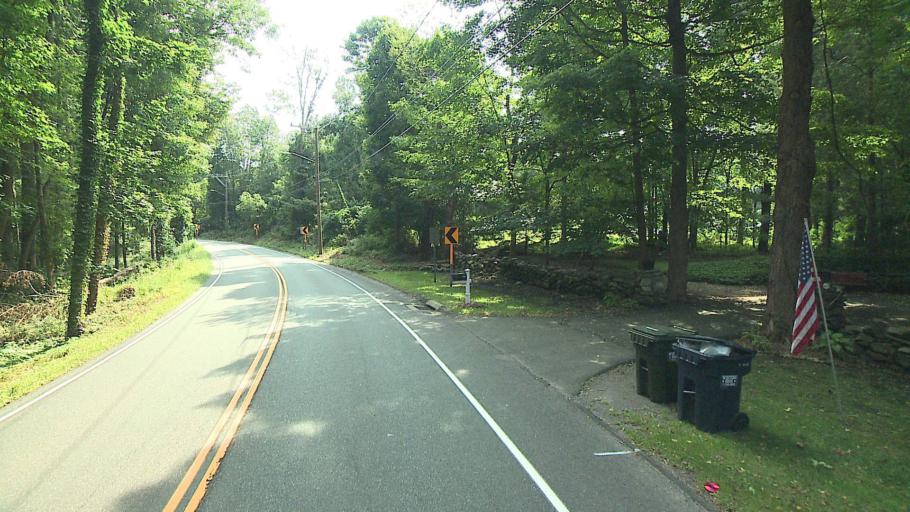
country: US
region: Connecticut
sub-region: Fairfield County
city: Ridgefield
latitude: 41.2660
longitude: -73.5121
